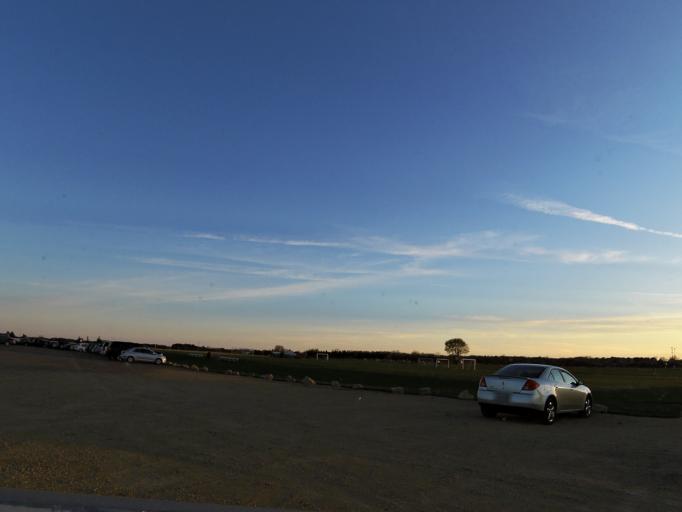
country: US
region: Minnesota
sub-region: Washington County
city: Lakeland
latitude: 44.9537
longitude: -92.7893
